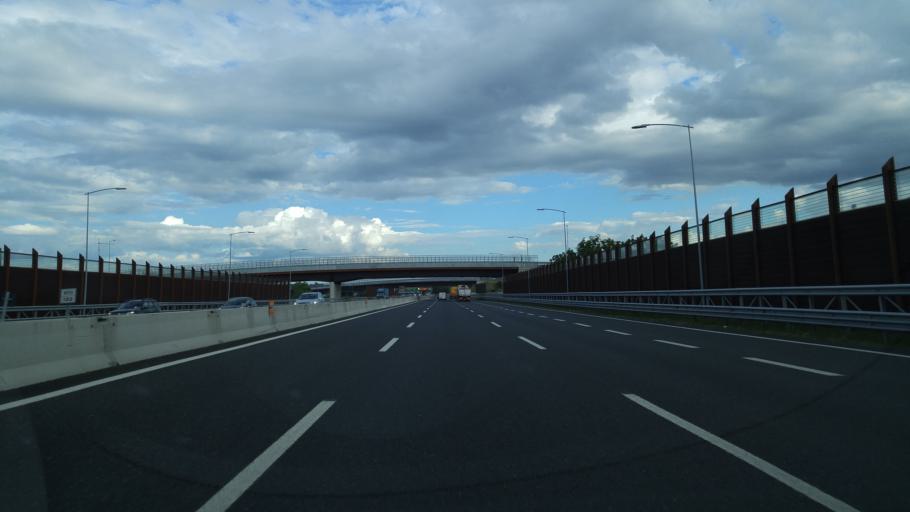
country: IT
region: Emilia-Romagna
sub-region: Provincia di Rimini
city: Coriano
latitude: 43.9936
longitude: 12.6210
